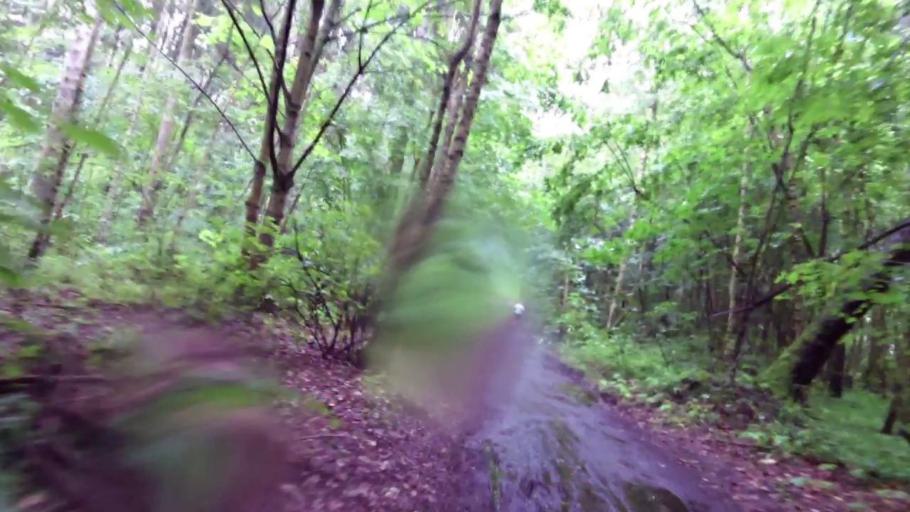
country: PL
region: West Pomeranian Voivodeship
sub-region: Powiat koszalinski
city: Mielno
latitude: 54.2556
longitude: 16.0301
